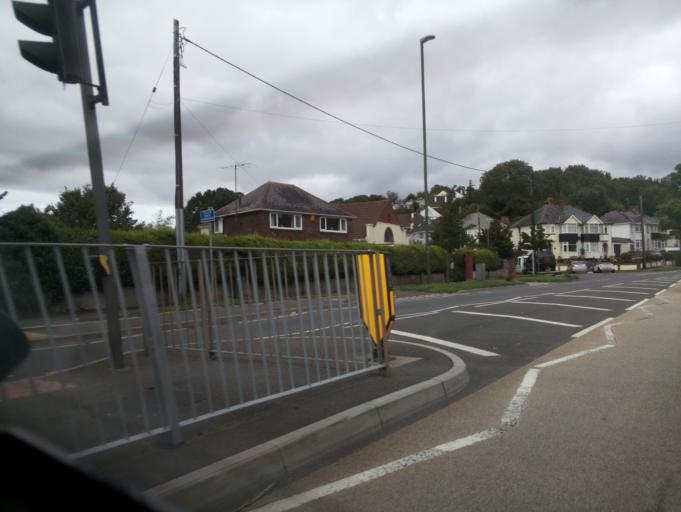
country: GB
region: England
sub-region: Borough of Torbay
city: Paignton
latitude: 50.4320
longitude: -3.5892
